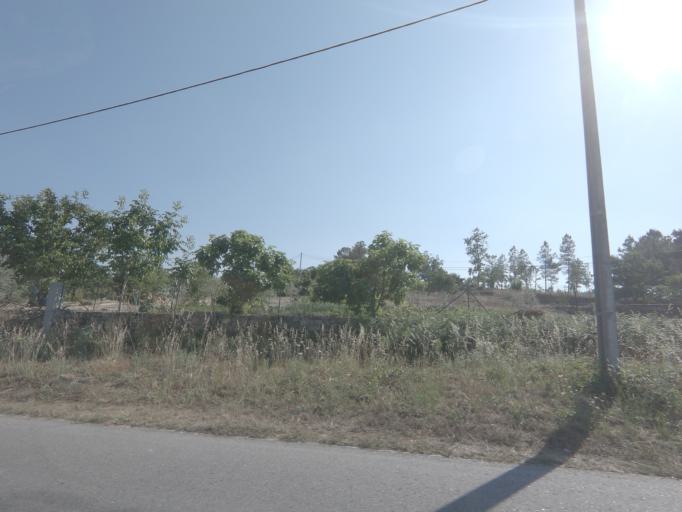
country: PT
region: Viseu
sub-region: Moimenta da Beira
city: Moimenta da Beira
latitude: 40.9990
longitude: -7.5591
